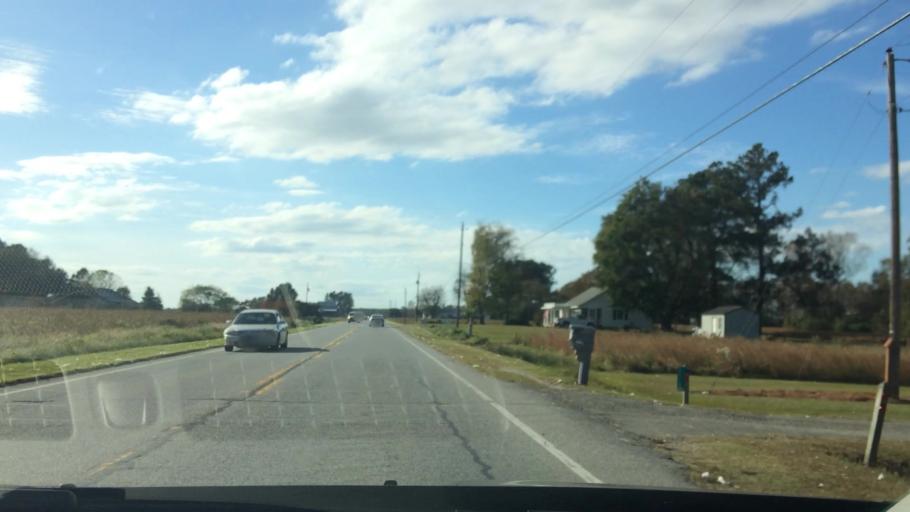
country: US
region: North Carolina
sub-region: Greene County
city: Snow Hill
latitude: 35.4416
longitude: -77.7994
